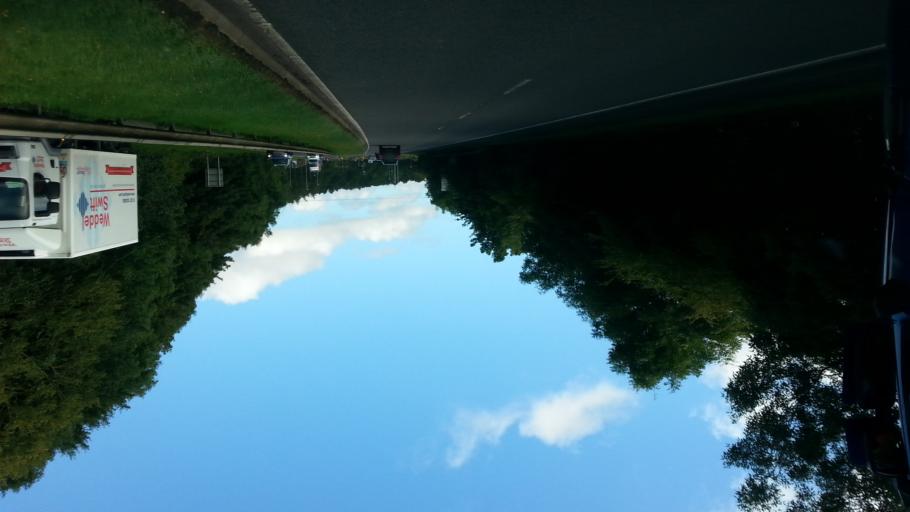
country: GB
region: England
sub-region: Northamptonshire
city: Corby
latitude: 52.4837
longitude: -0.6572
